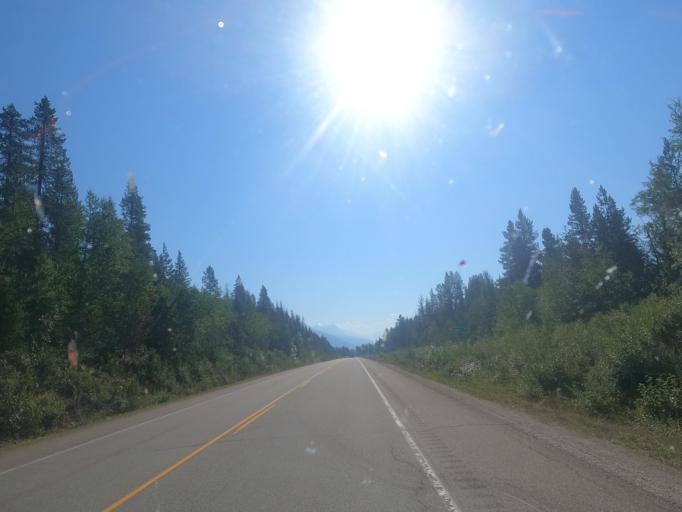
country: CA
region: Alberta
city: Jasper Park Lodge
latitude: 52.9760
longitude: -118.9631
